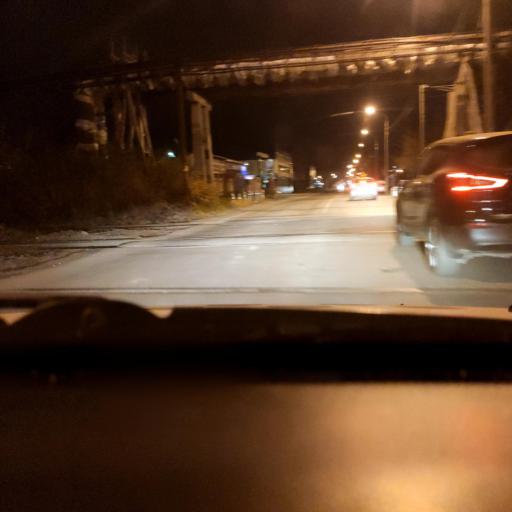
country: RU
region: Perm
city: Perm
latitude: 57.9673
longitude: 56.2541
